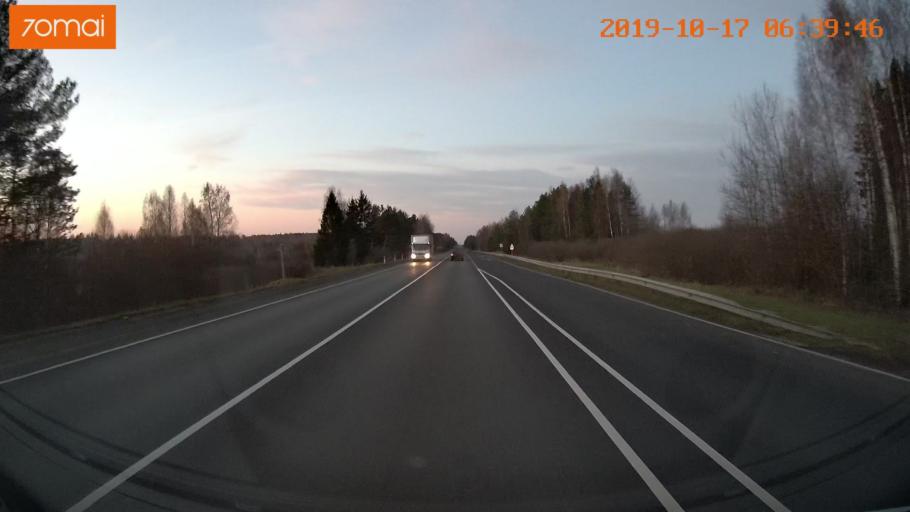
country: RU
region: Ivanovo
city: Novoye Leushino
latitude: 56.6387
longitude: 40.5759
